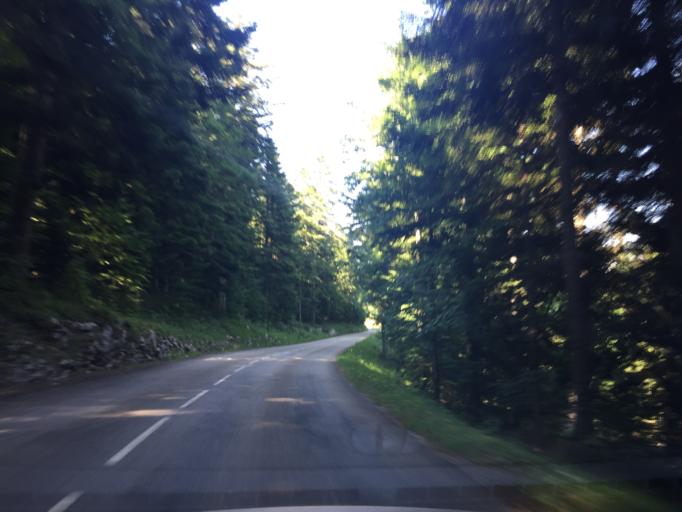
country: FR
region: Rhone-Alpes
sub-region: Departement de la Drome
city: Saint-Jean-en-Royans
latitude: 44.9430
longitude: 5.3093
